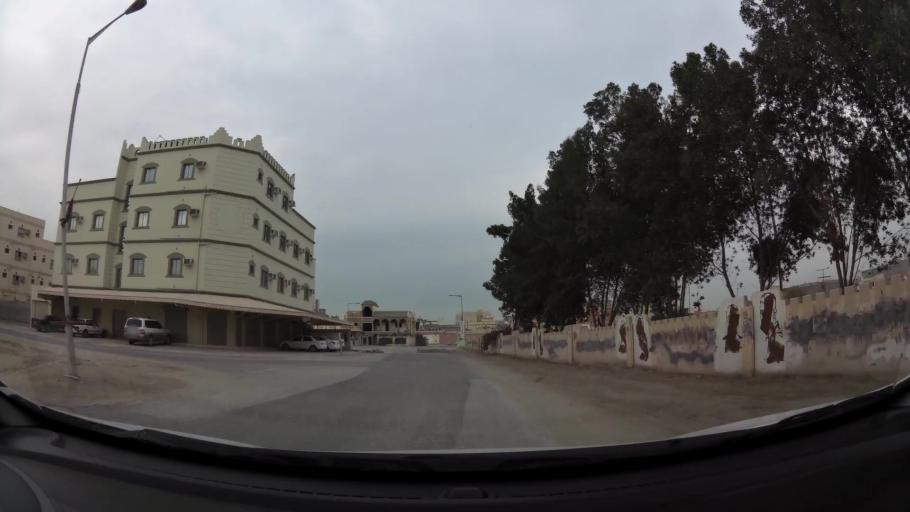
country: BH
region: Northern
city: Sitrah
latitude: 26.1439
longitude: 50.6088
